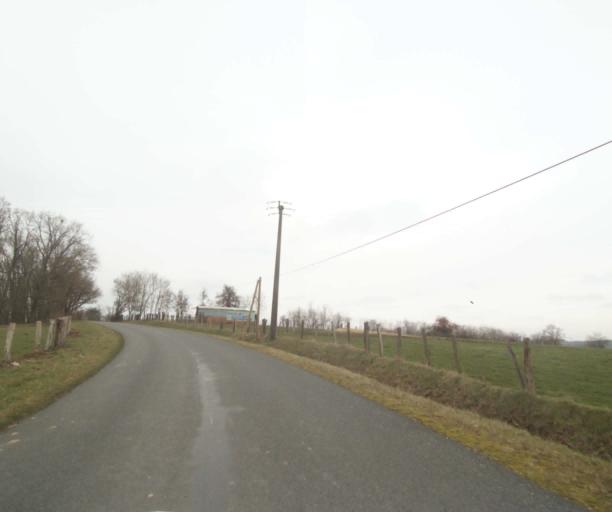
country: FR
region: Champagne-Ardenne
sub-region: Departement de la Marne
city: Pargny-sur-Saulx
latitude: 48.7430
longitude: 4.8419
